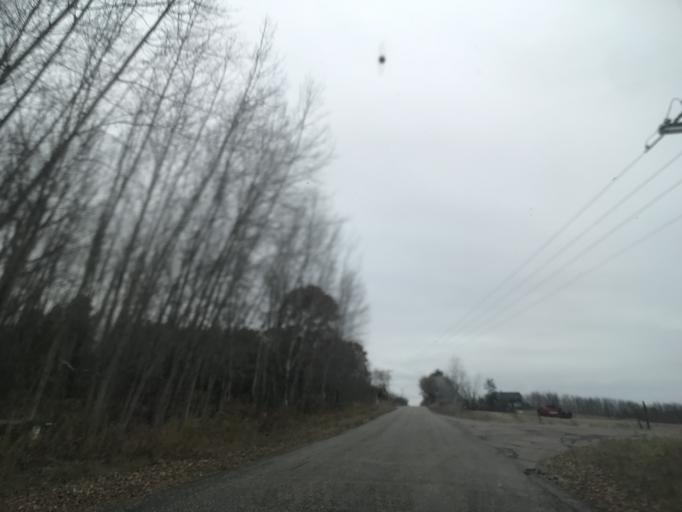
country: US
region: Wisconsin
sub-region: Menominee County
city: Legend Lake
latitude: 45.1703
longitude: -88.4558
